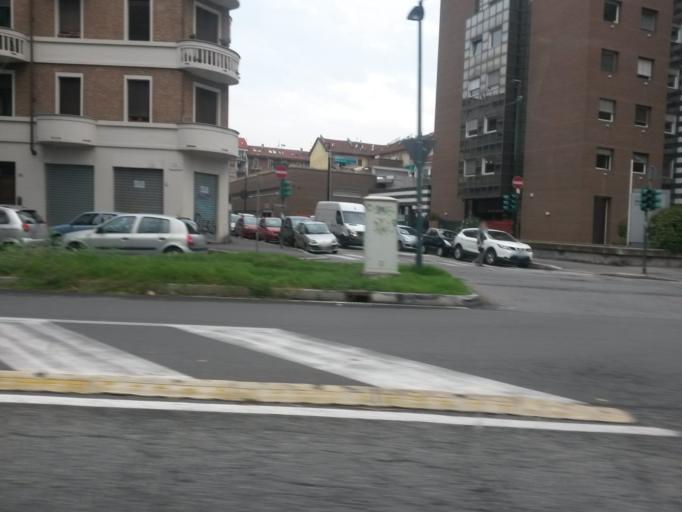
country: IT
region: Piedmont
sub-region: Provincia di Torino
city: Lesna
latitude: 45.0737
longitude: 7.6419
